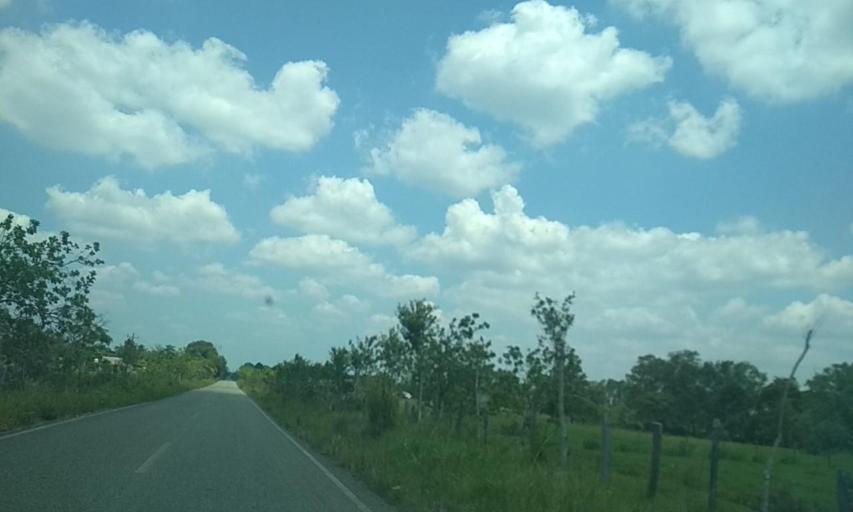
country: MX
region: Tabasco
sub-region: Huimanguillo
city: Huapacal 1ra. Seccion
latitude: 17.7539
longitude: -93.7478
